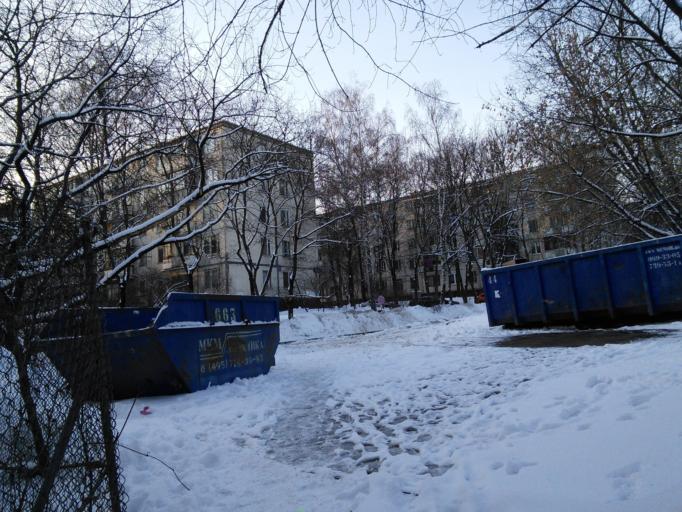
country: RU
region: Moscow
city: Davydkovo
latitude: 55.7226
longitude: 37.4745
